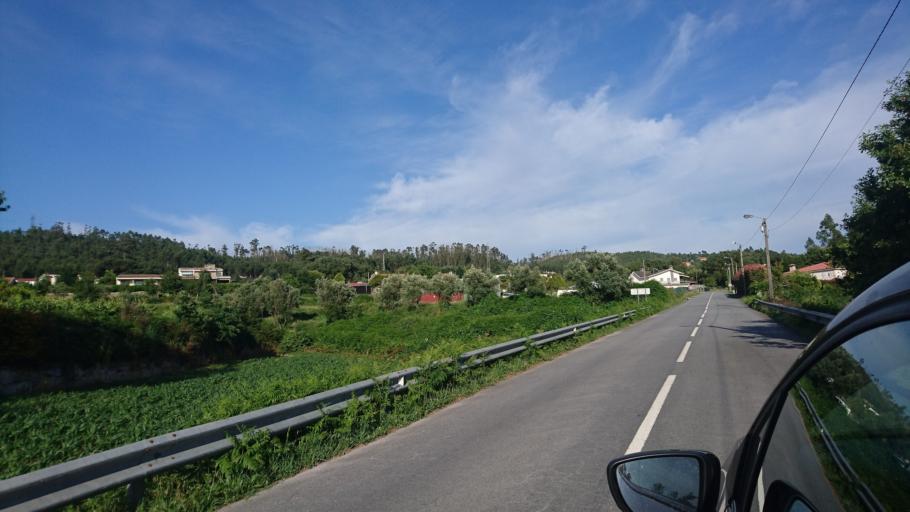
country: PT
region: Porto
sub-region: Paredes
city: Recarei
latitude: 41.1363
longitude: -8.3792
